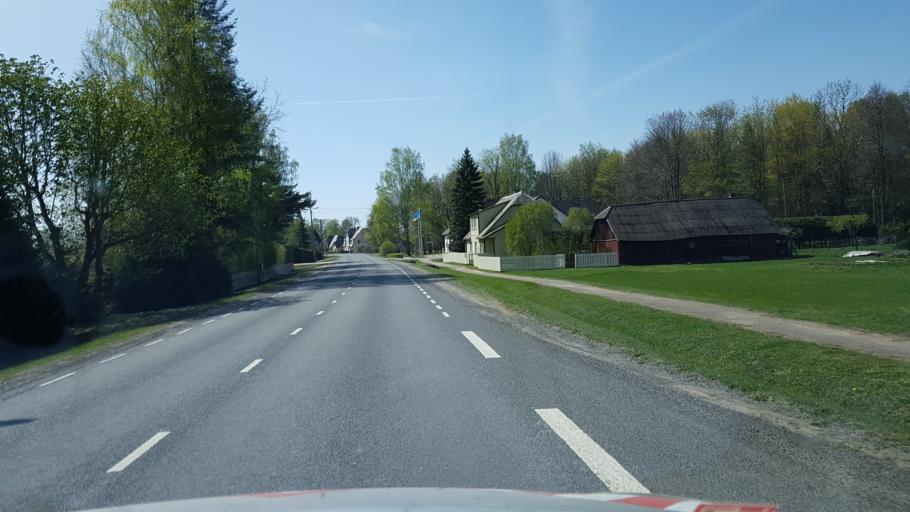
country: EE
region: Tartu
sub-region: Noo vald
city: Noo
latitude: 58.2803
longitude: 26.5430
